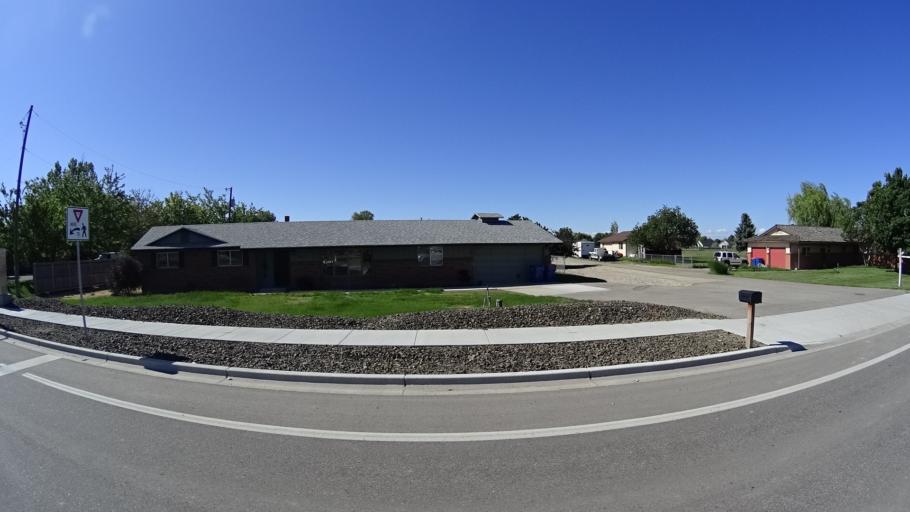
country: US
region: Idaho
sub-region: Ada County
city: Meridian
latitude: 43.6337
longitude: -116.3987
